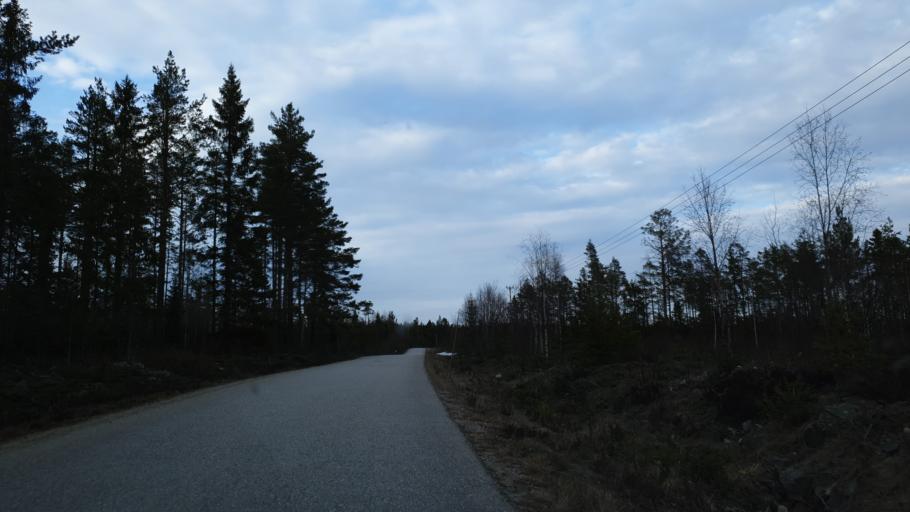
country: SE
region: Vaesternorrland
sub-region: Sundsvalls Kommun
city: Njurundabommen
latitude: 62.0064
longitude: 17.3920
